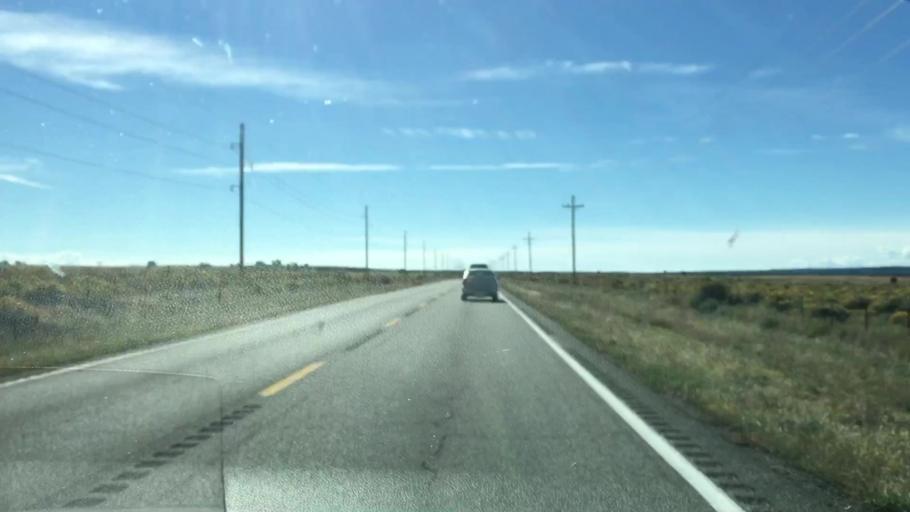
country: US
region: Arizona
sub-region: Mohave County
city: Colorado City
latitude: 37.0701
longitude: -113.1039
